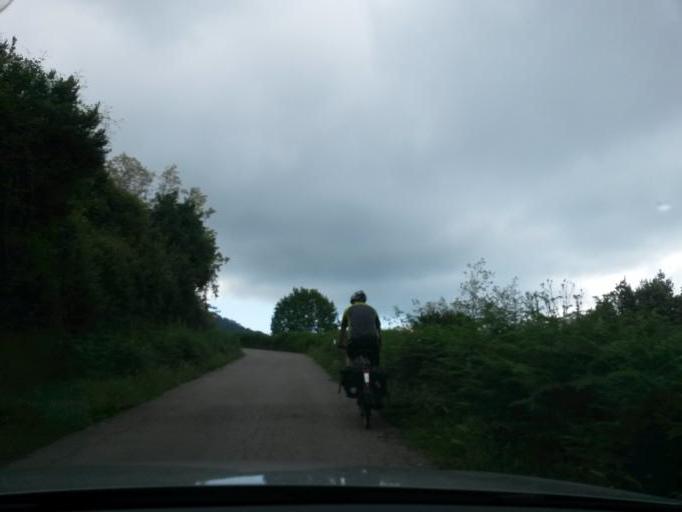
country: IT
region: Tuscany
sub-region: Provincia di Livorno
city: Campo nell'Elba
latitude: 42.7615
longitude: 10.1979
